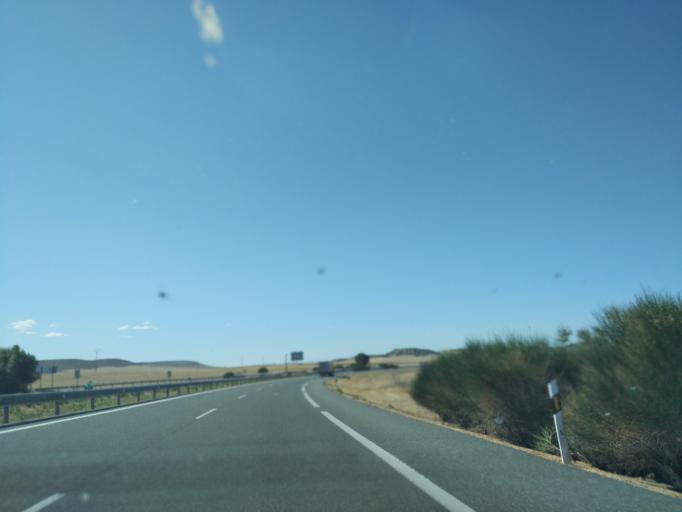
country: ES
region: Castille and Leon
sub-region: Provincia de Valladolid
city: Mota del Marques
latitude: 41.6309
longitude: -5.1851
